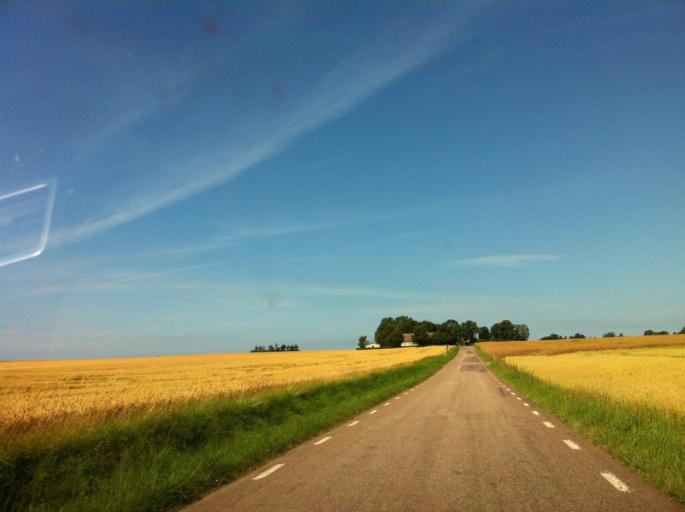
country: SE
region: Skane
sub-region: Helsingborg
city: Glumslov
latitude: 55.9386
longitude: 12.8495
